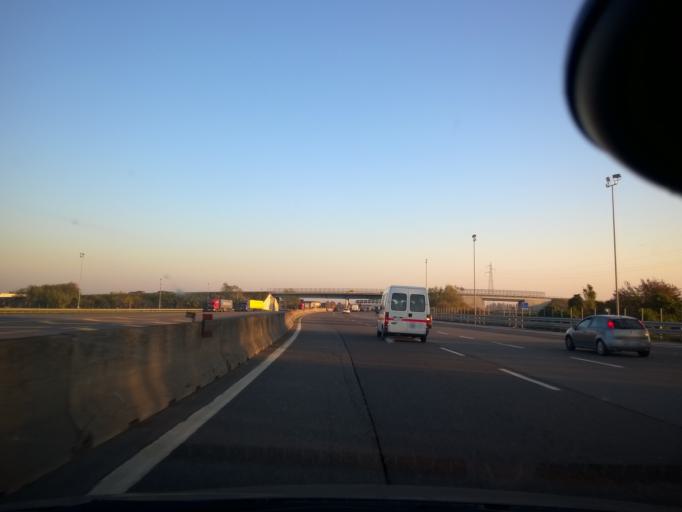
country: IT
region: Lombardy
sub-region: Citta metropolitana di Milano
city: Riozzo
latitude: 45.3481
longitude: 9.3108
